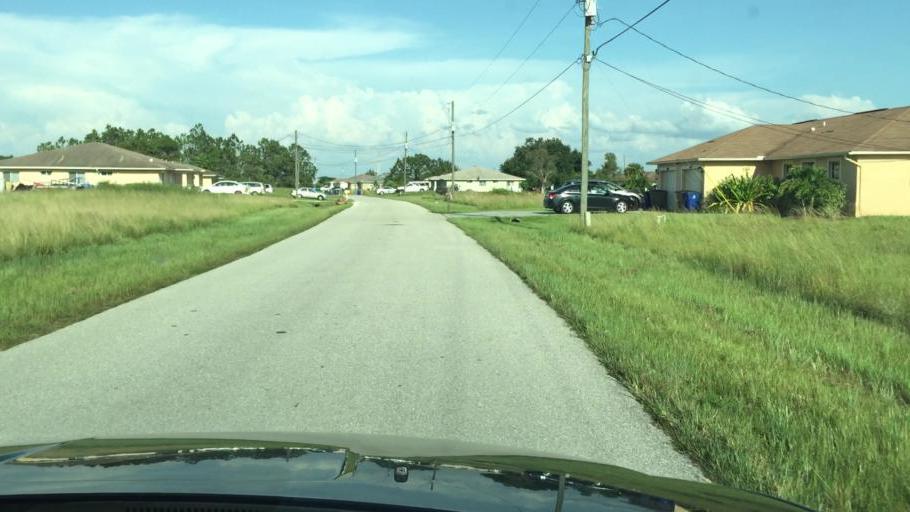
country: US
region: Florida
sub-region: Lee County
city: Gateway
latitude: 26.5891
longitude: -81.7174
